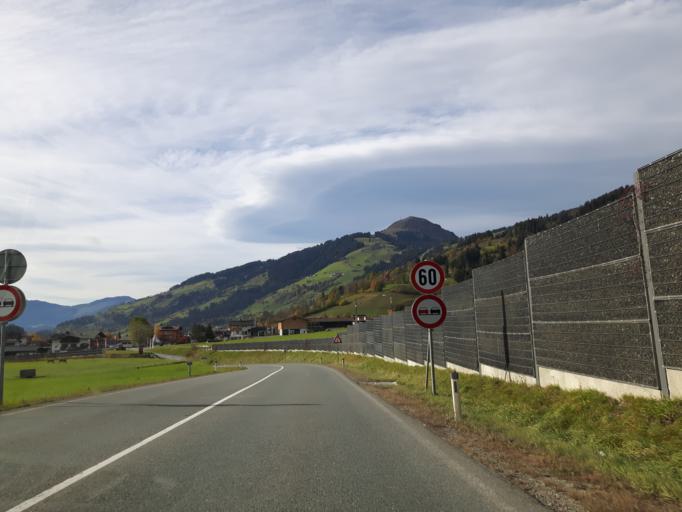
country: AT
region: Tyrol
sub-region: Politischer Bezirk Kitzbuhel
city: Brixen im Thale
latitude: 47.4507
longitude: 12.2703
